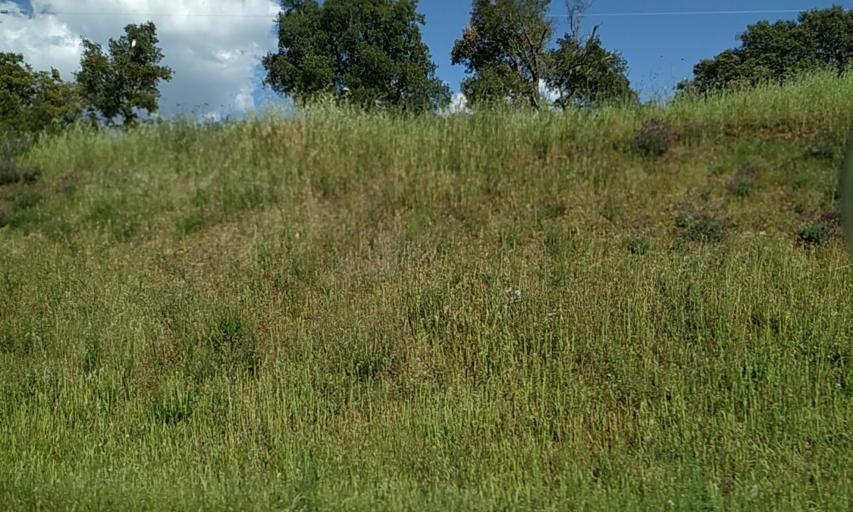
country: PT
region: Evora
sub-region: Estremoz
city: Estremoz
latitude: 38.8808
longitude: -7.5597
